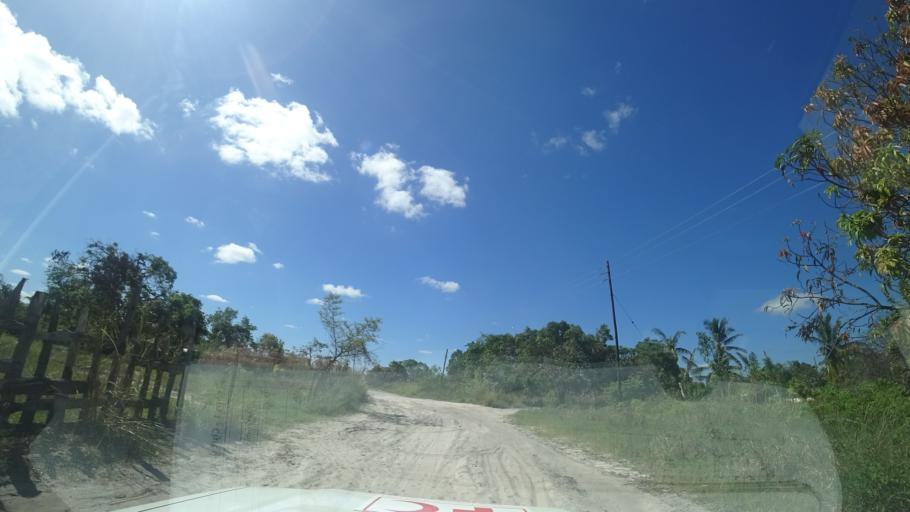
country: MZ
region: Sofala
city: Dondo
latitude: -19.5044
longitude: 34.6115
